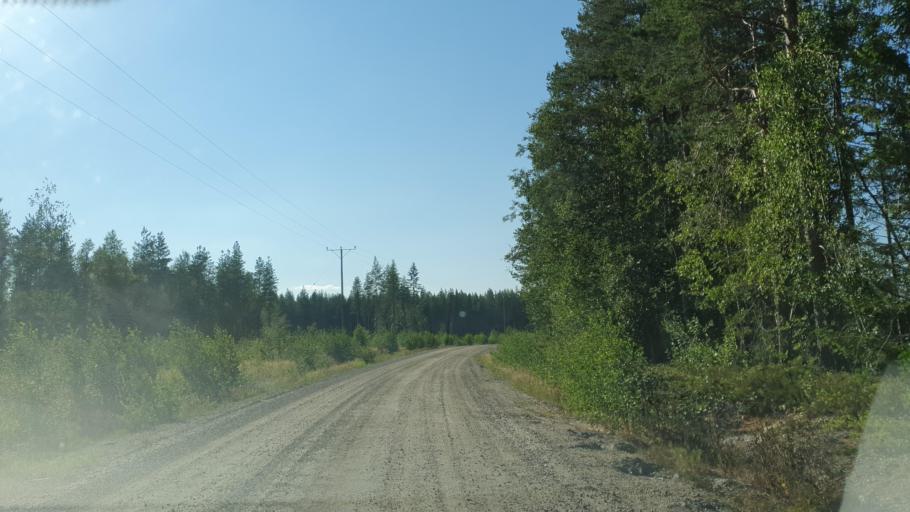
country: FI
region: Kainuu
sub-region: Kehys-Kainuu
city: Kuhmo
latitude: 64.0323
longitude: 29.6842
